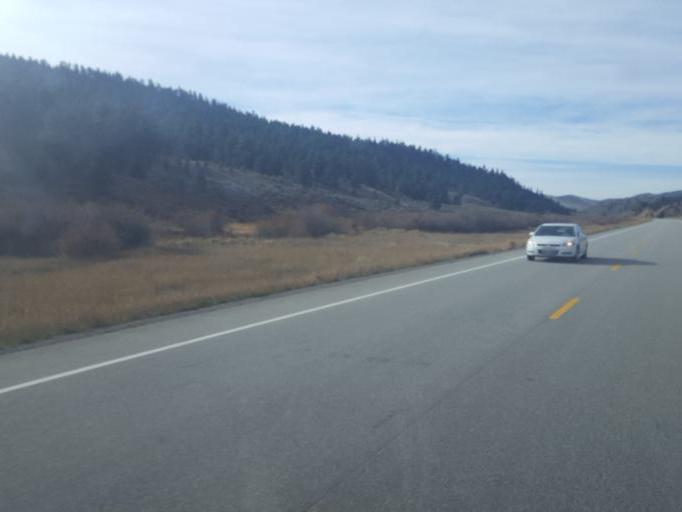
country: US
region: Colorado
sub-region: Costilla County
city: San Luis
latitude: 37.5429
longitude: -105.2871
